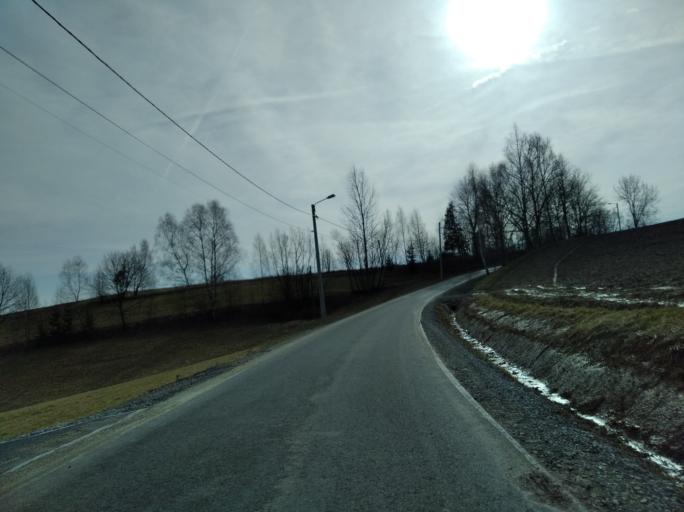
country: PL
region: Subcarpathian Voivodeship
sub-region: Powiat brzozowski
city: Jasienica Rosielna
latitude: 49.7645
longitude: 21.9445
